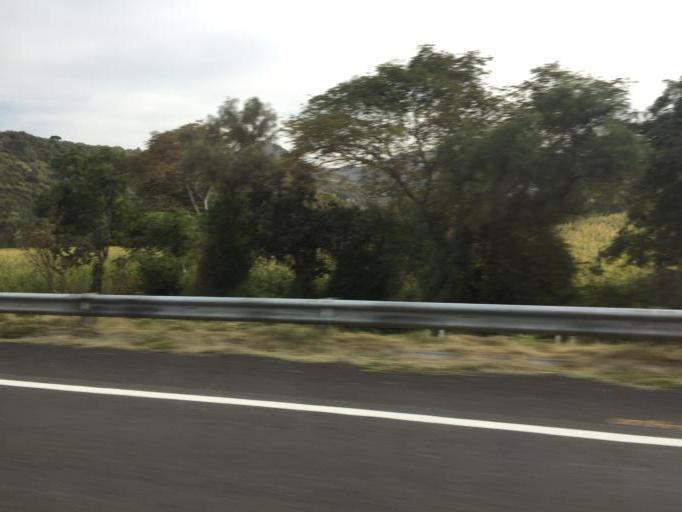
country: MX
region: Michoacan
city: Copandaro de Galeana
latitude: 19.8842
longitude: -101.2250
